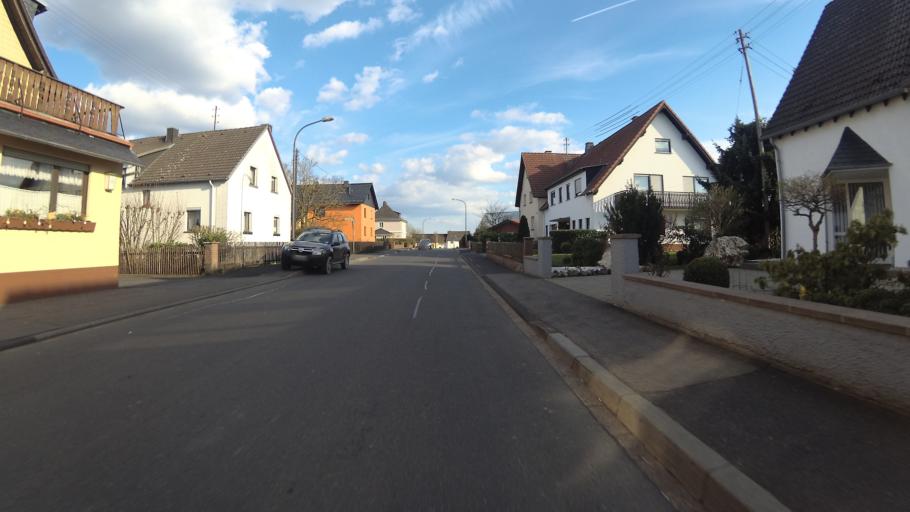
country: DE
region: Rheinland-Pfalz
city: Darscheid
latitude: 50.2141
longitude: 6.8896
